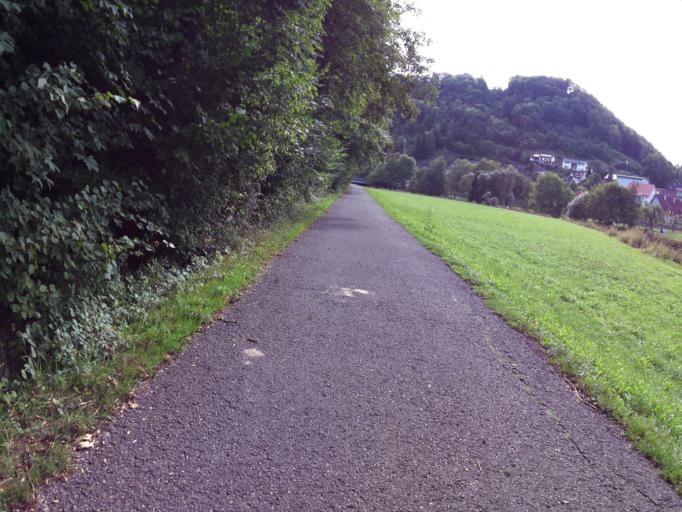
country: DE
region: Baden-Wuerttemberg
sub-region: Freiburg Region
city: Epfendorf
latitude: 48.2244
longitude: 8.6010
